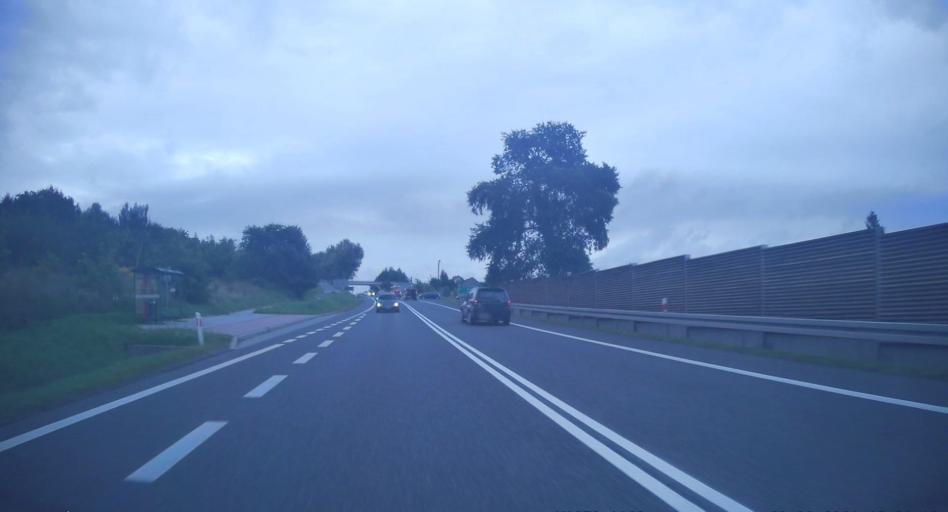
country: PL
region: Lesser Poland Voivodeship
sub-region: Powiat wielicki
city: Szarow
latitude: 49.9824
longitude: 20.2307
